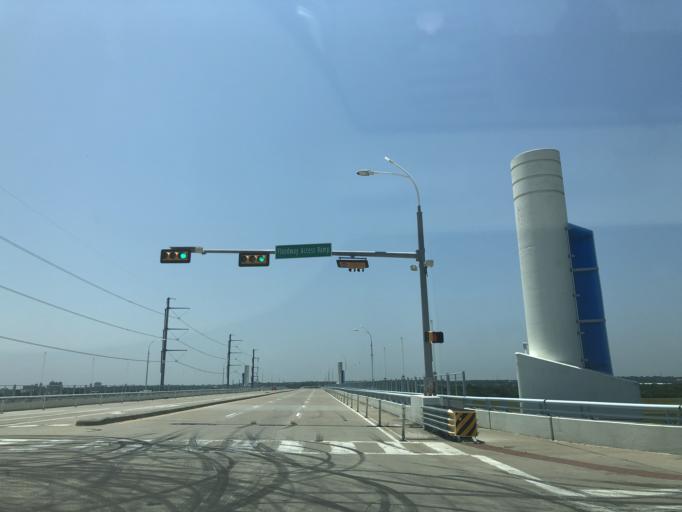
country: US
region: Texas
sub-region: Dallas County
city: Dallas
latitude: 32.7909
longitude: -96.8349
